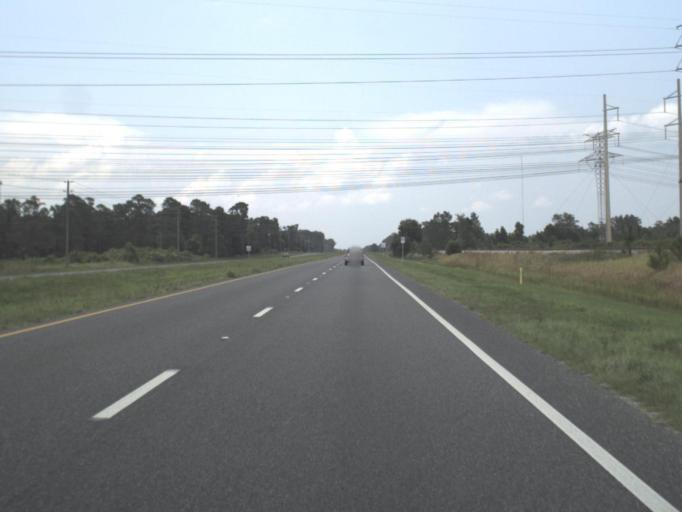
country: US
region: Florida
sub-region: Putnam County
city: Palatka
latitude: 29.7263
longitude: -81.6519
